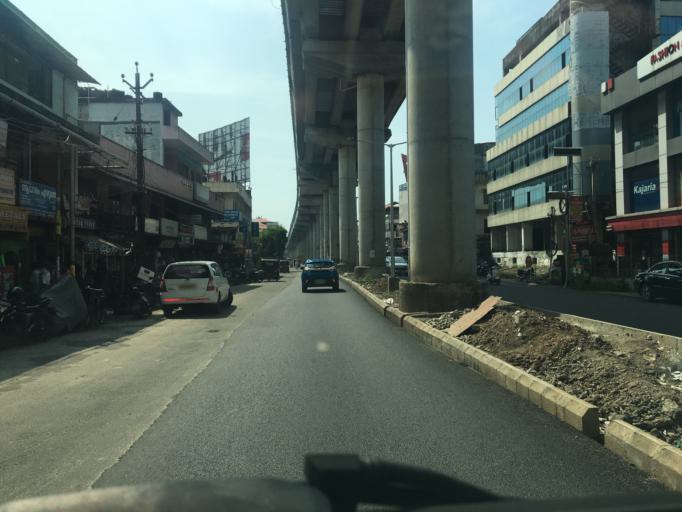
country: IN
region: Kerala
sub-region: Ernakulam
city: Cochin
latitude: 9.9688
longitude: 76.3167
